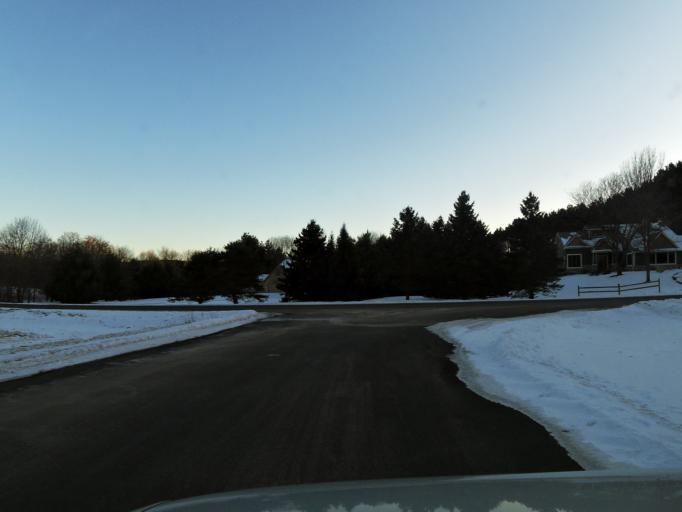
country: US
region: Minnesota
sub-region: Washington County
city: Lake Elmo
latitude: 44.9871
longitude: -92.8315
